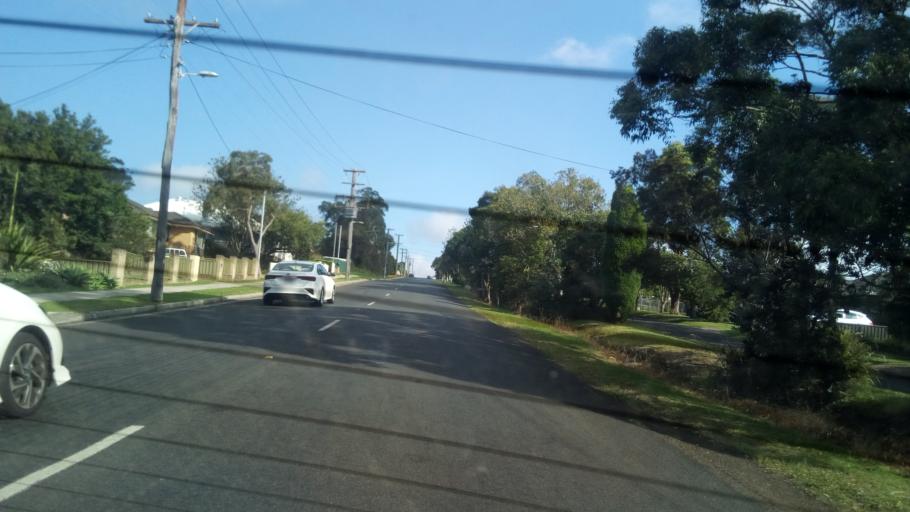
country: AU
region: New South Wales
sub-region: Wollongong
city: Helensburgh
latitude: -34.1971
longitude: 150.9808
